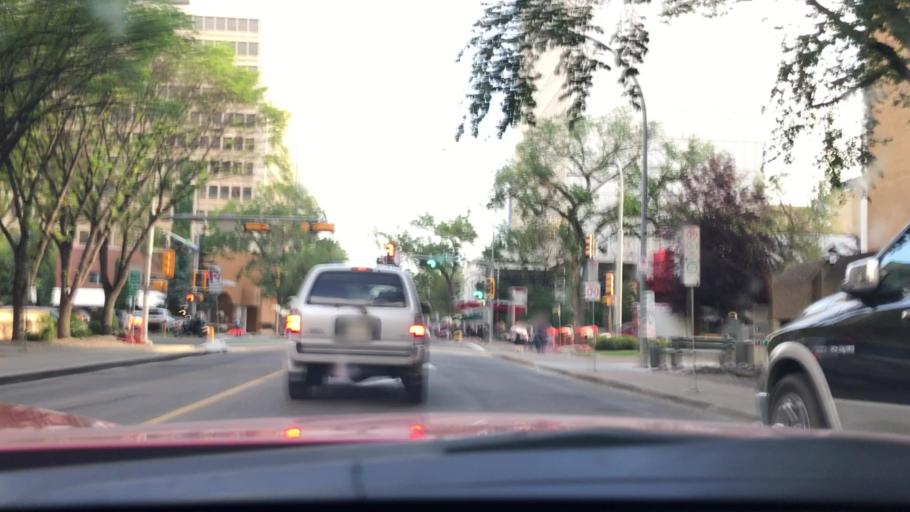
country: CA
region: Alberta
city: Edmonton
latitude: 53.5383
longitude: -113.5048
